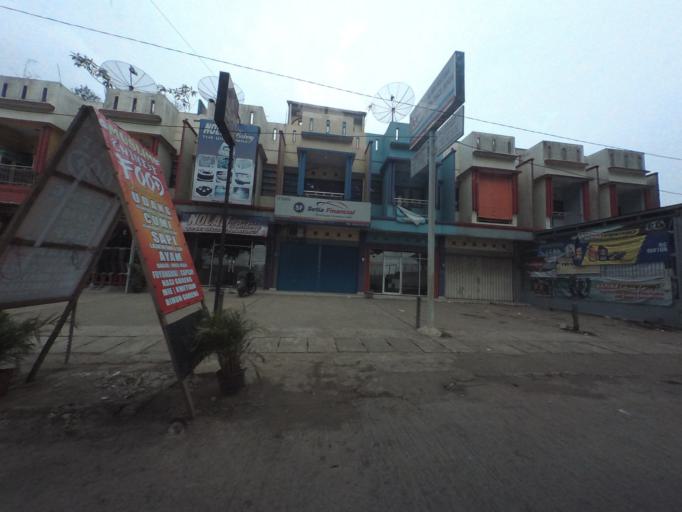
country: ID
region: West Java
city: Cicurug
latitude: -6.7594
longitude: 106.7996
